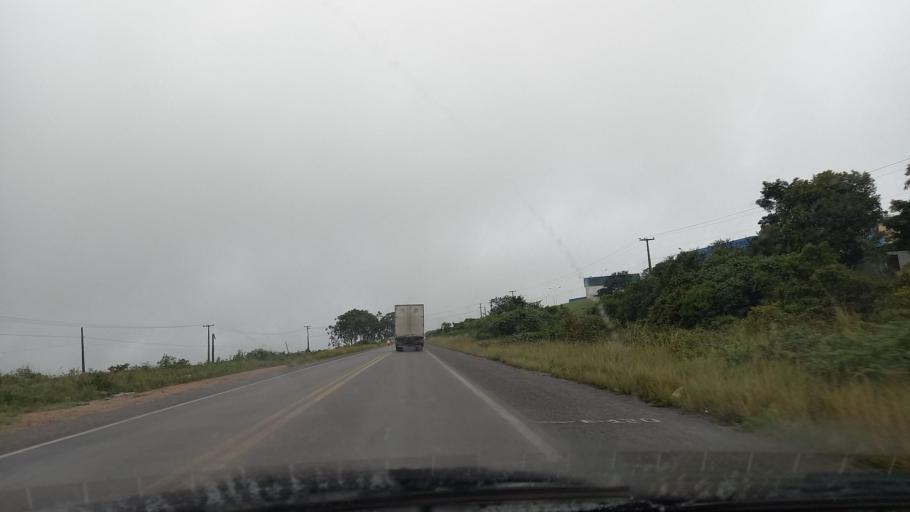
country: BR
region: Pernambuco
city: Garanhuns
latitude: -8.8746
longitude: -36.5276
